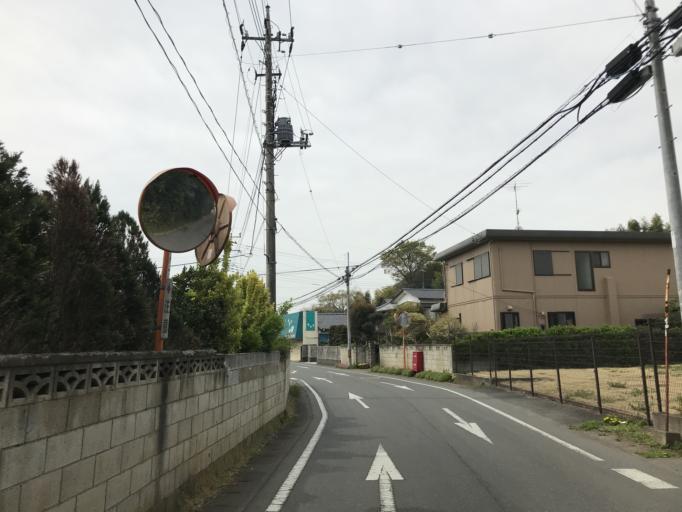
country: JP
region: Ibaraki
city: Moriya
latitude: 35.9402
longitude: 140.0062
